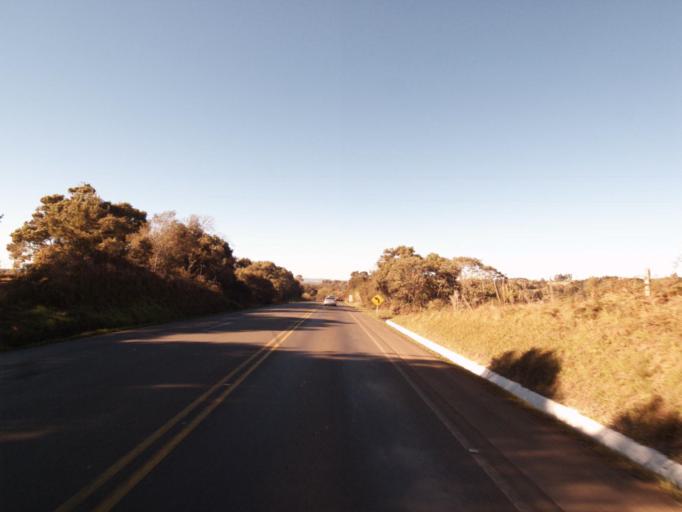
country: BR
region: Santa Catarina
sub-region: Concordia
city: Concordia
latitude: -26.8957
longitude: -51.9787
